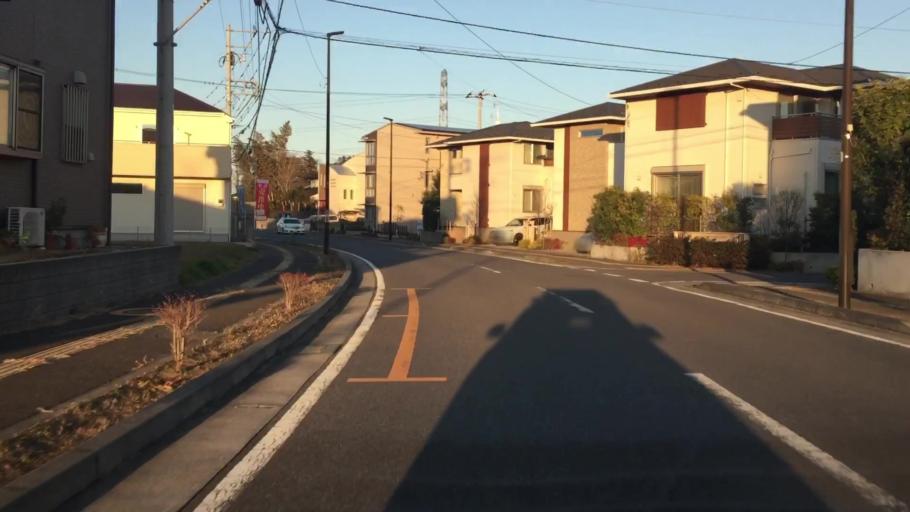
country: JP
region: Ibaraki
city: Moriya
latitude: 35.9152
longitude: 139.9547
